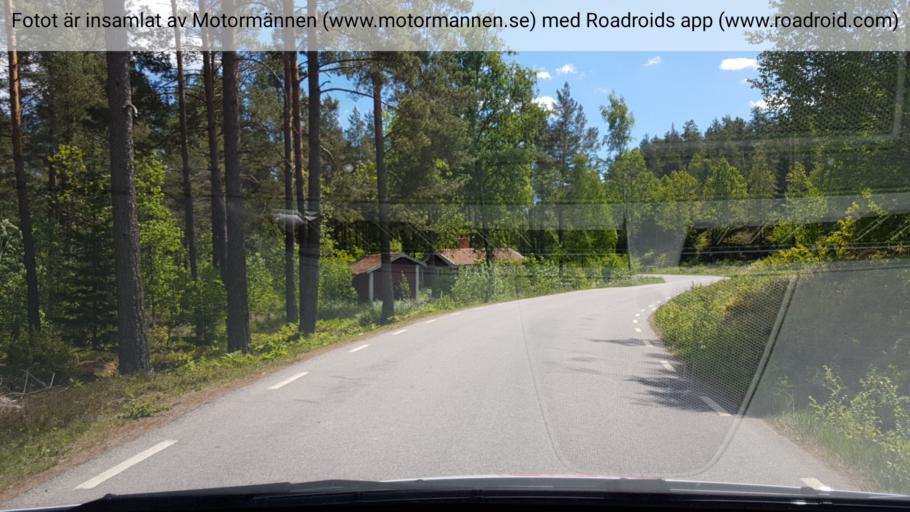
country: SE
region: Kalmar
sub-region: Vasterviks Kommun
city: Vaestervik
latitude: 57.9337
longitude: 16.6781
